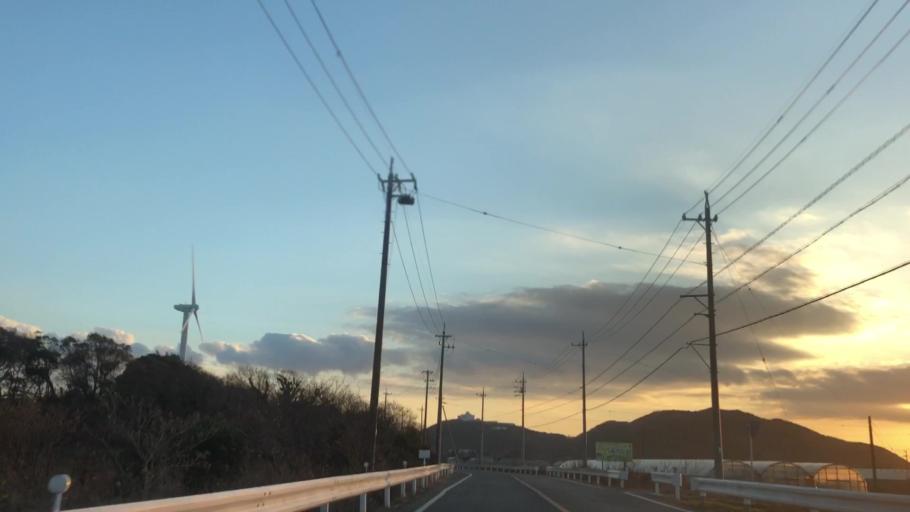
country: JP
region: Aichi
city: Toyohama
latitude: 34.5982
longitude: 137.0496
